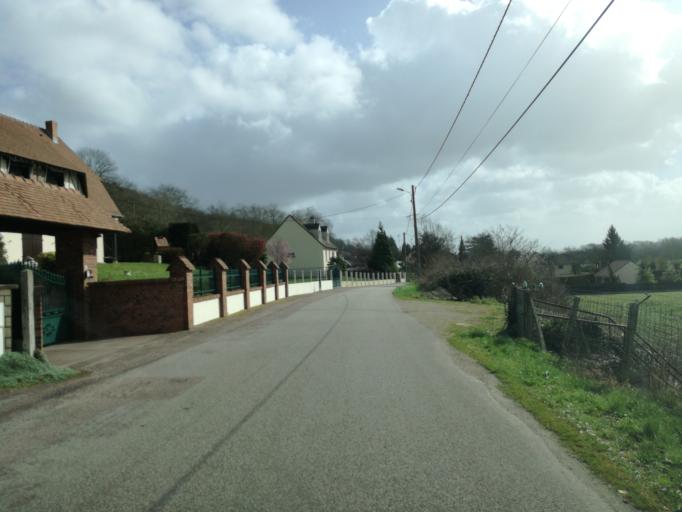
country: FR
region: Haute-Normandie
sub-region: Departement de la Seine-Maritime
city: La Mailleraye-sur-Seine
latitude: 49.5060
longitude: 0.7831
